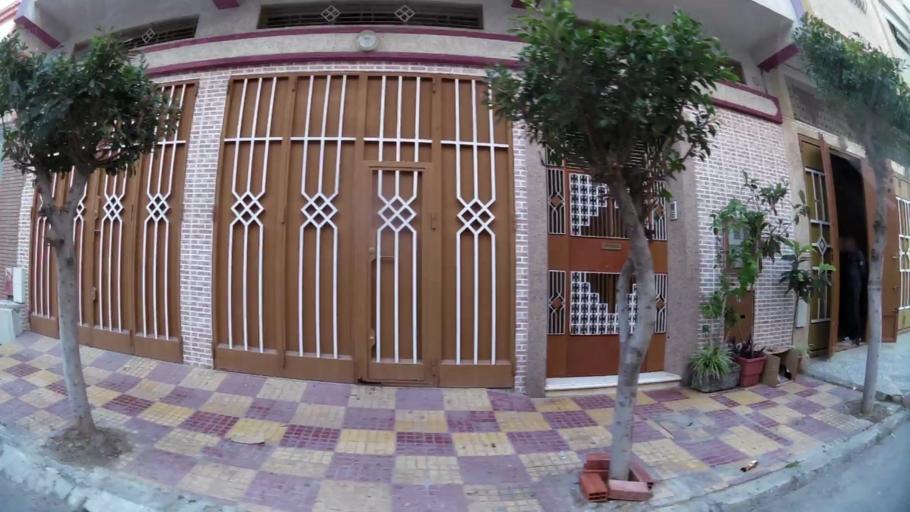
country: MA
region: Tanger-Tetouan
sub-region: Tanger-Assilah
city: Tangier
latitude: 35.7521
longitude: -5.7977
